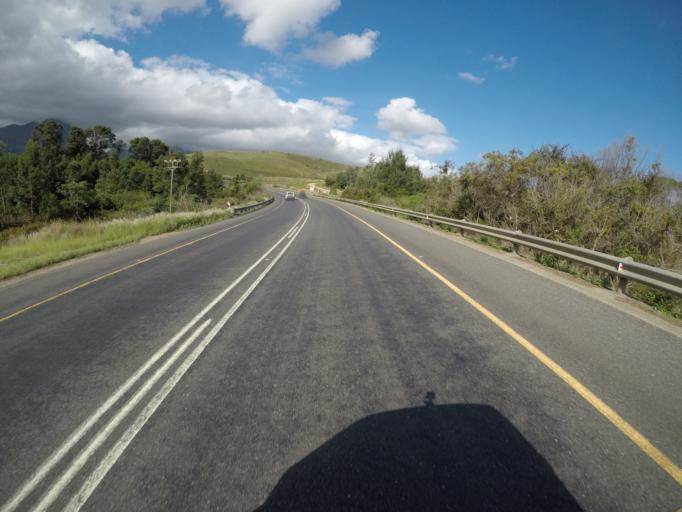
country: ZA
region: Western Cape
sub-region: Overberg District Municipality
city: Swellendam
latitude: -34.0030
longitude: 20.3325
